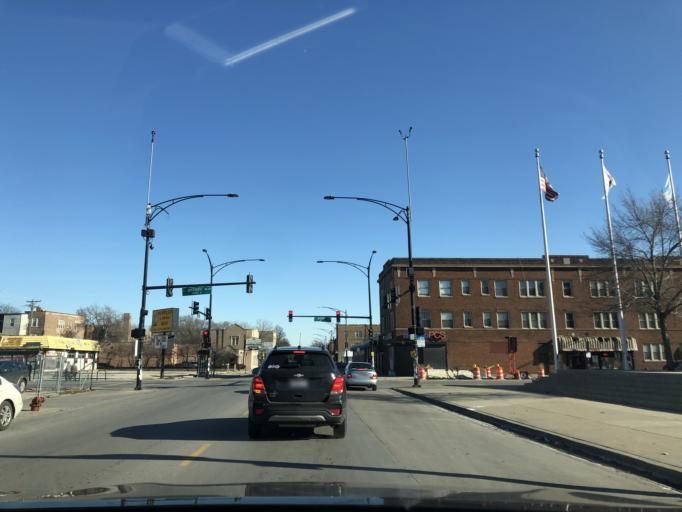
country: US
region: Indiana
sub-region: Lake County
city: Whiting
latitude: 41.7589
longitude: -87.5767
